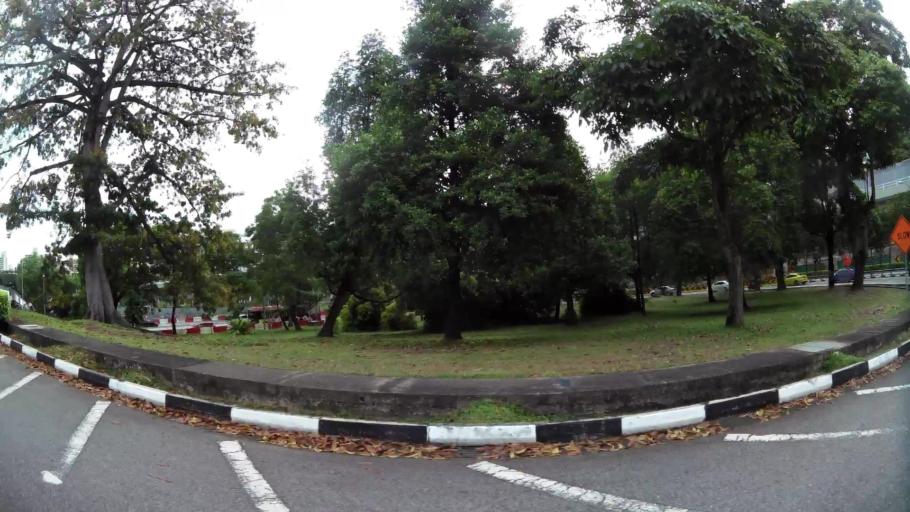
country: SG
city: Singapore
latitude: 1.3440
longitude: 103.8535
